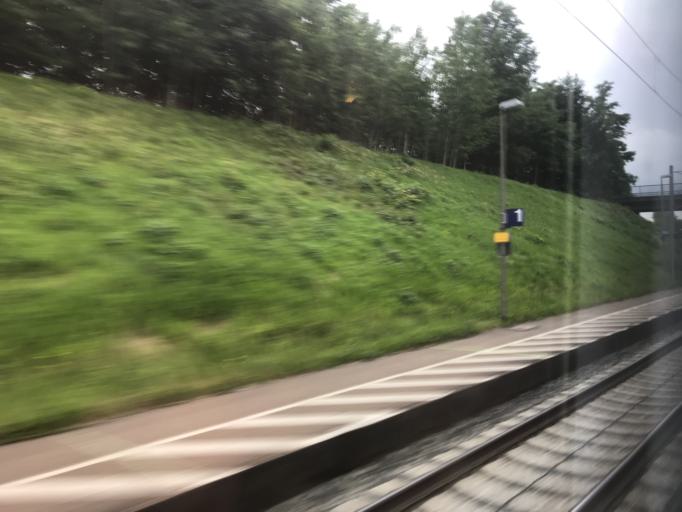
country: DE
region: Bavaria
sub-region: Swabia
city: Kutzenhausen
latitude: 48.3347
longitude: 10.6985
